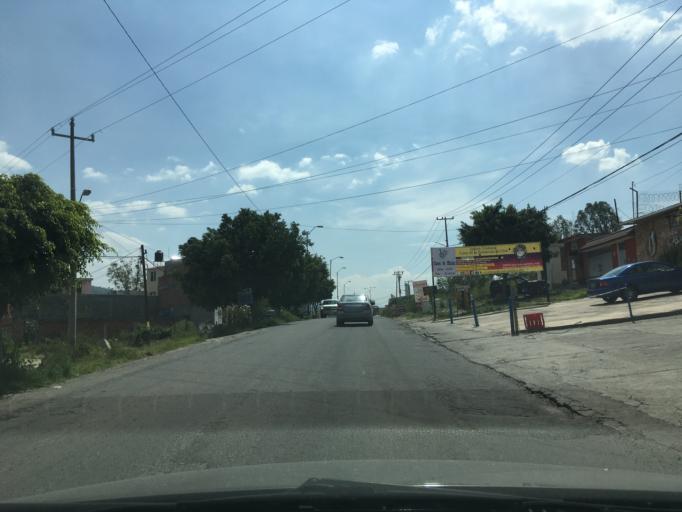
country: MX
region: Michoacan
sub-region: Morelia
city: Montana Monarca (Punta Altozano)
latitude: 19.6589
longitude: -101.2008
